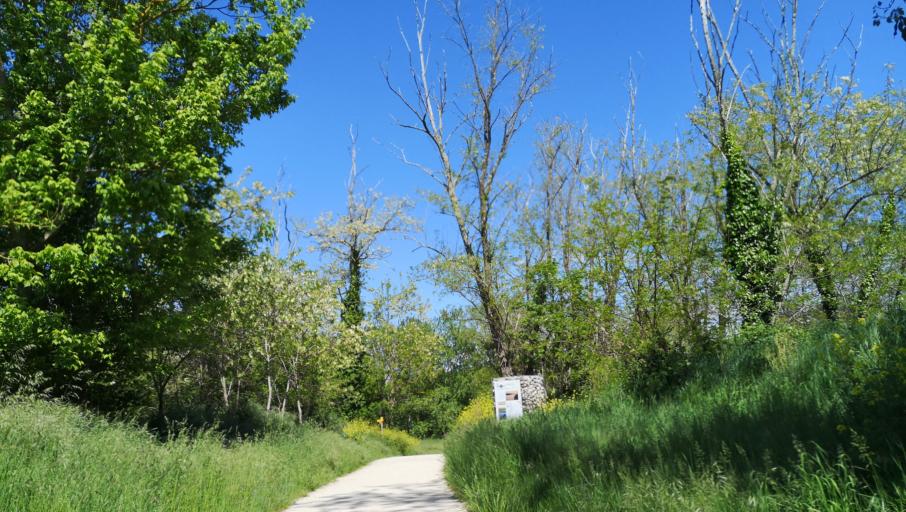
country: FR
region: Midi-Pyrenees
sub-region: Departement de la Haute-Garonne
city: Seilh
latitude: 43.6920
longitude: 1.3657
